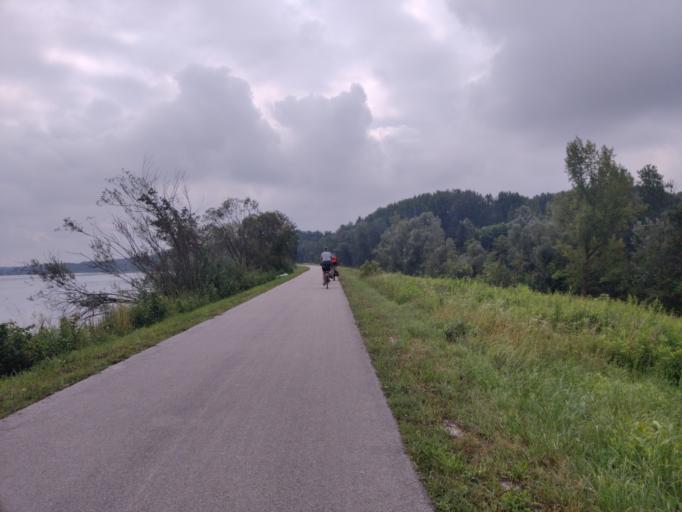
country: AT
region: Lower Austria
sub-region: Politischer Bezirk Sankt Polten
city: Traismauer
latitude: 48.3720
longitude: 15.7381
